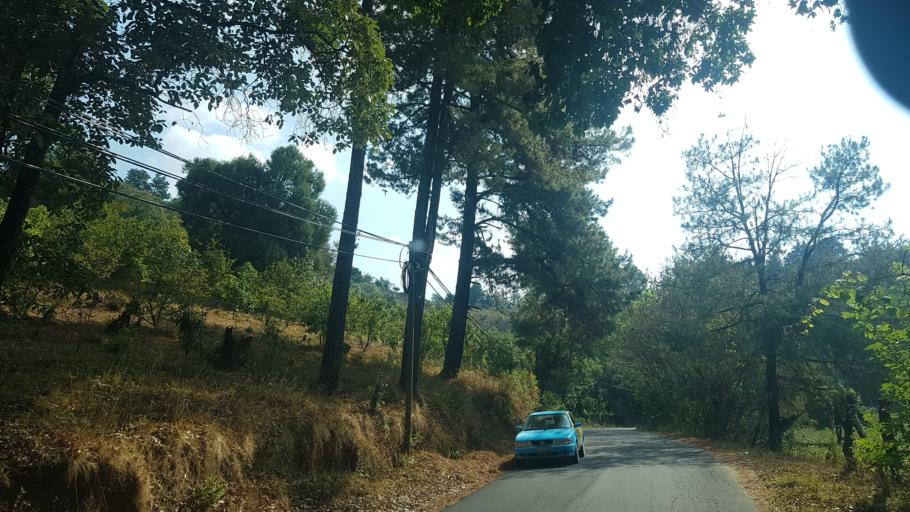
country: MX
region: Morelos
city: Hueyapan
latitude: 18.8777
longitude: -98.6984
